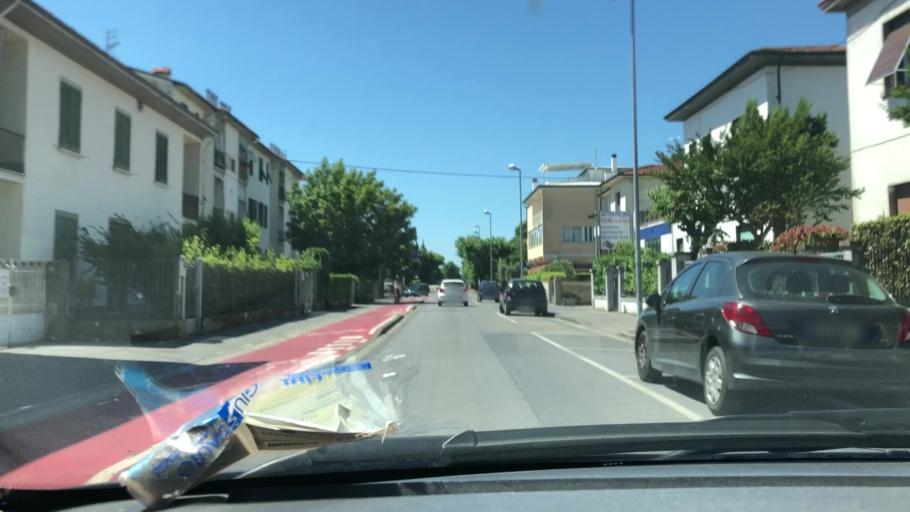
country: IT
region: Tuscany
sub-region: Province of Pisa
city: Pontedera
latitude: 43.6569
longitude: 10.6322
